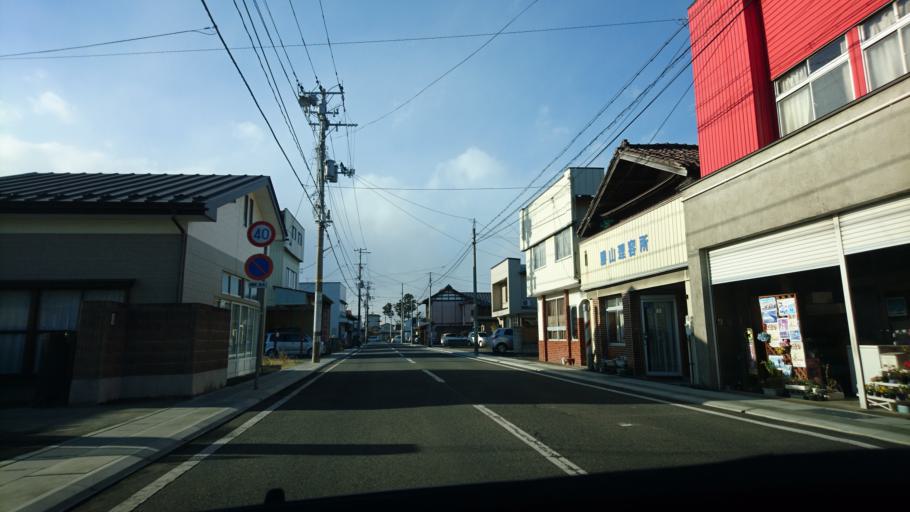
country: JP
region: Iwate
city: Mizusawa
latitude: 39.1468
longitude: 141.1420
